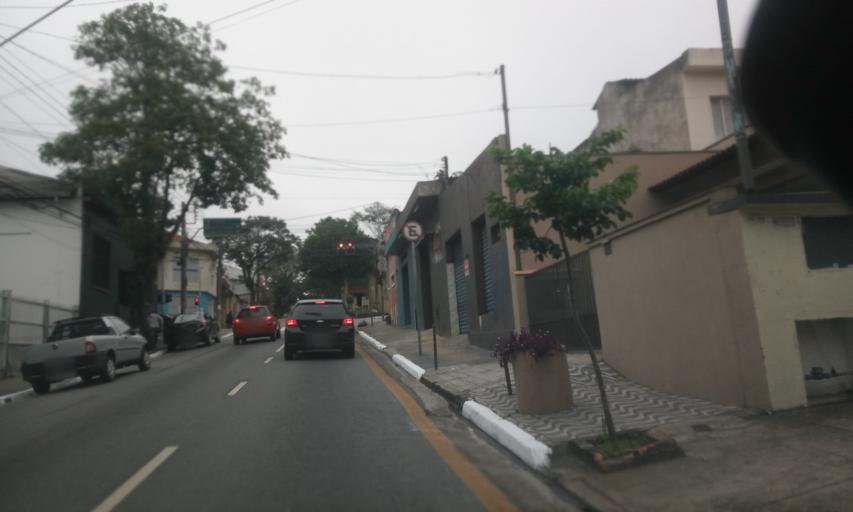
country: BR
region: Sao Paulo
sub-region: Sao Caetano Do Sul
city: Sao Caetano do Sul
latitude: -23.6285
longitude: -46.5693
